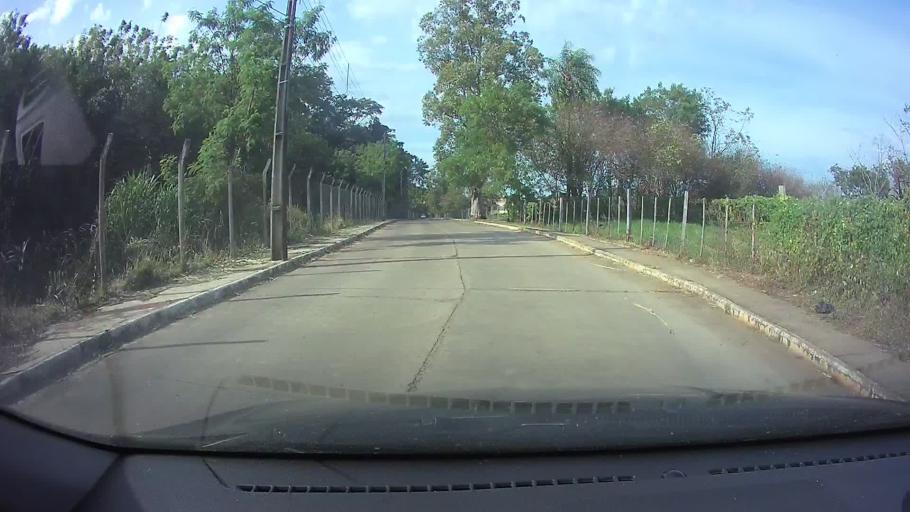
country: PY
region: Central
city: Fernando de la Mora
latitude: -25.3280
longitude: -57.5212
